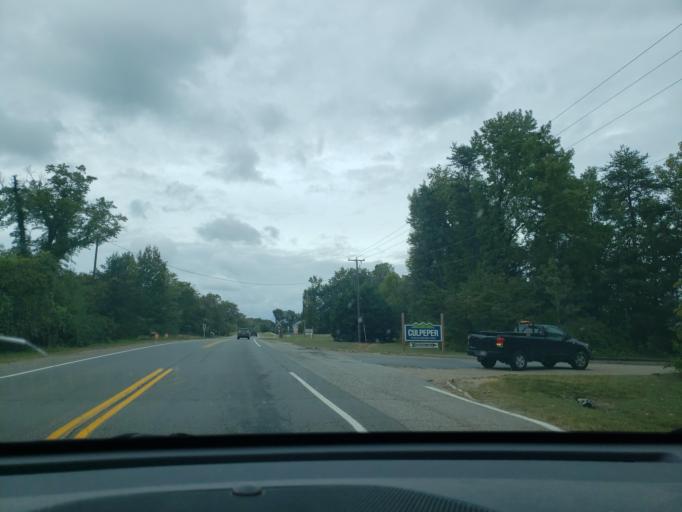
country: US
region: Virginia
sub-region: City of Fredericksburg
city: Fredericksburg
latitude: 38.2394
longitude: -77.4138
